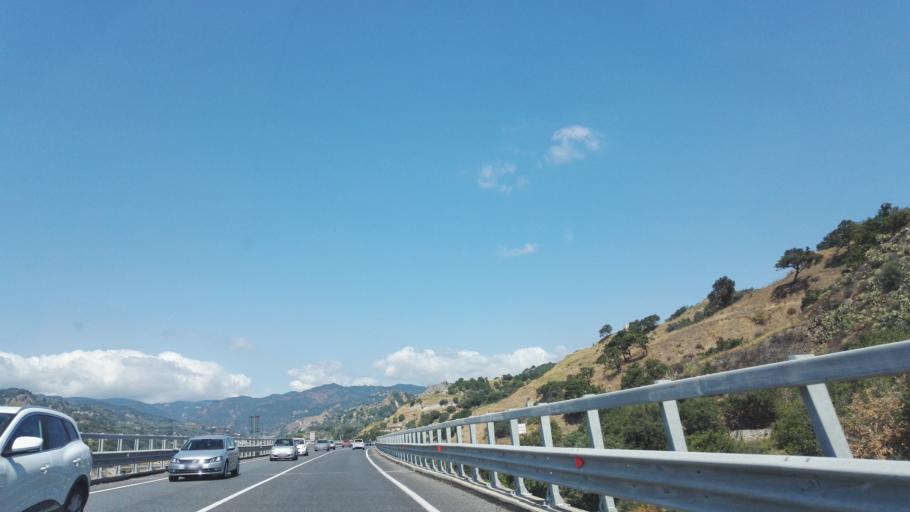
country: IT
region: Calabria
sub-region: Provincia di Reggio Calabria
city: Martone
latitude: 38.3380
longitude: 16.2810
